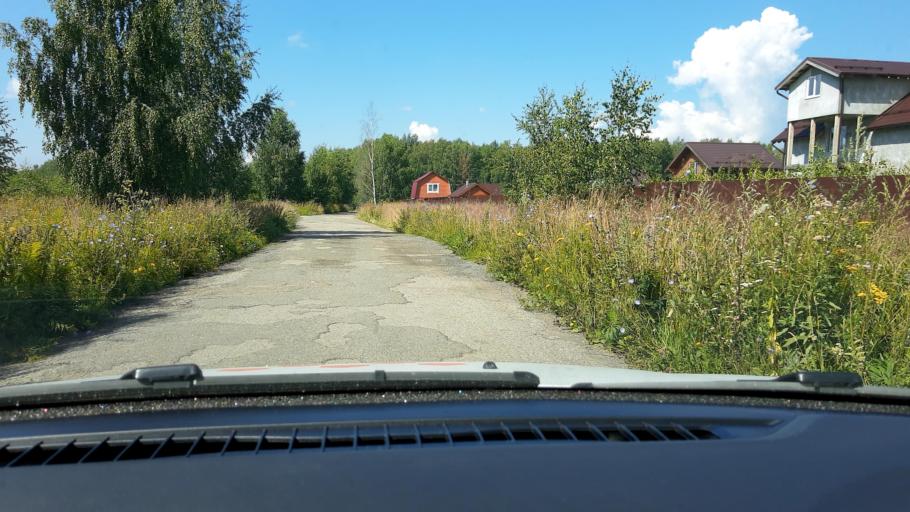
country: RU
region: Nizjnij Novgorod
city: Burevestnik
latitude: 56.0540
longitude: 43.9864
